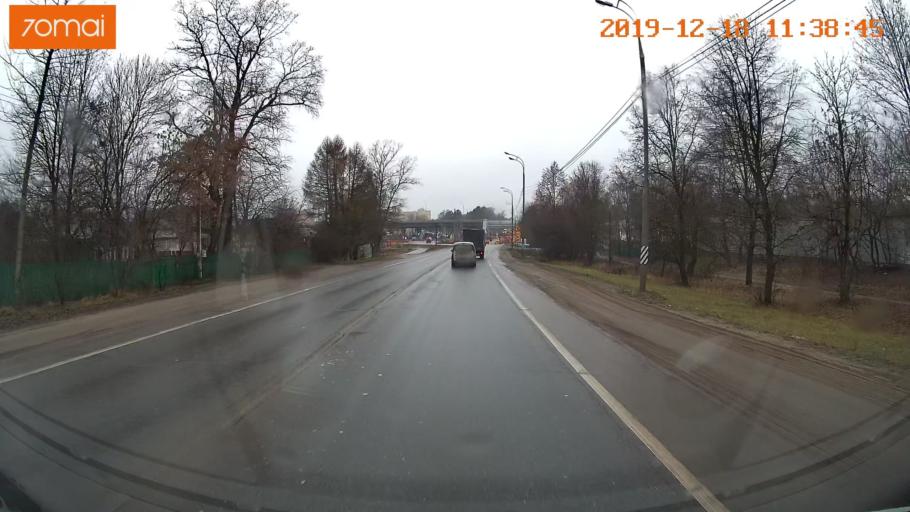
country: RU
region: Moskovskaya
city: Zvenigorod
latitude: 55.6982
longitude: 36.8854
